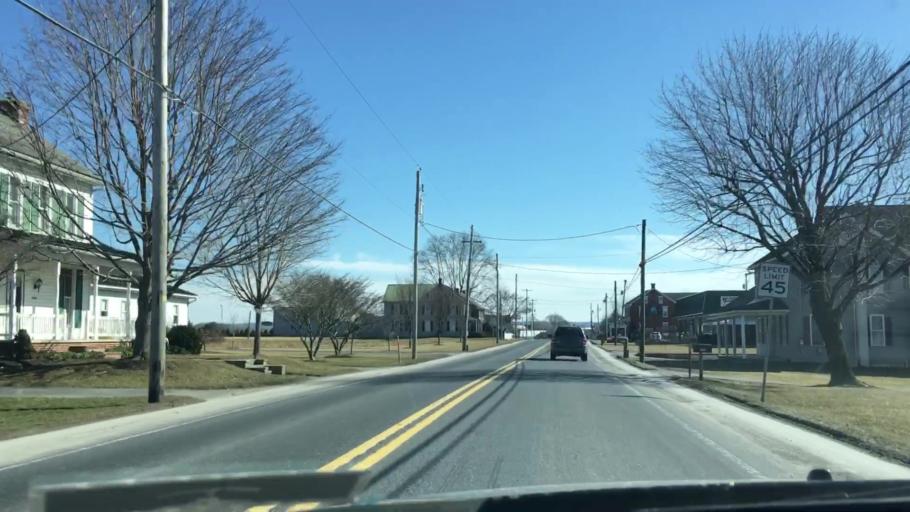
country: US
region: Pennsylvania
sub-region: Lancaster County
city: New Holland
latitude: 40.1493
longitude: -76.1226
